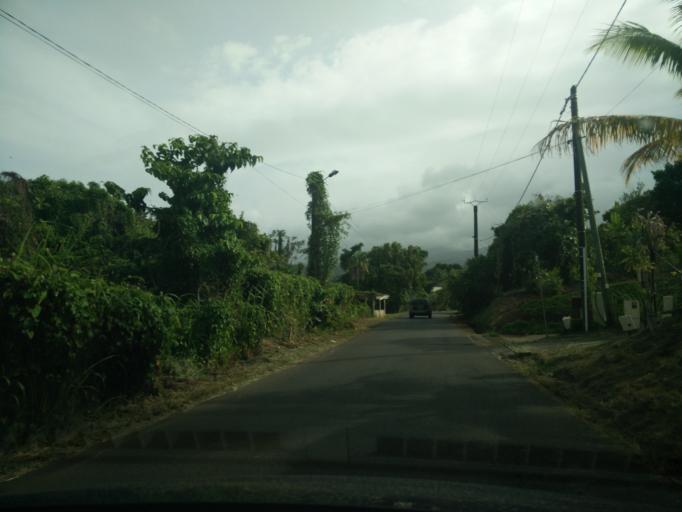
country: GP
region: Guadeloupe
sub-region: Guadeloupe
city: Petit-Bourg
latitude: 16.1276
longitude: -61.5897
